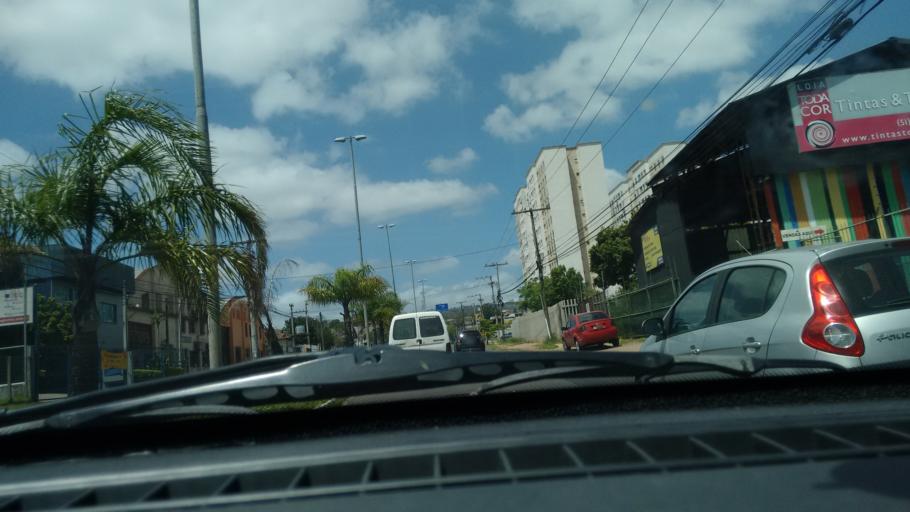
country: BR
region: Rio Grande do Sul
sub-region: Cachoeirinha
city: Cachoeirinha
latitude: -30.0180
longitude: -51.1195
